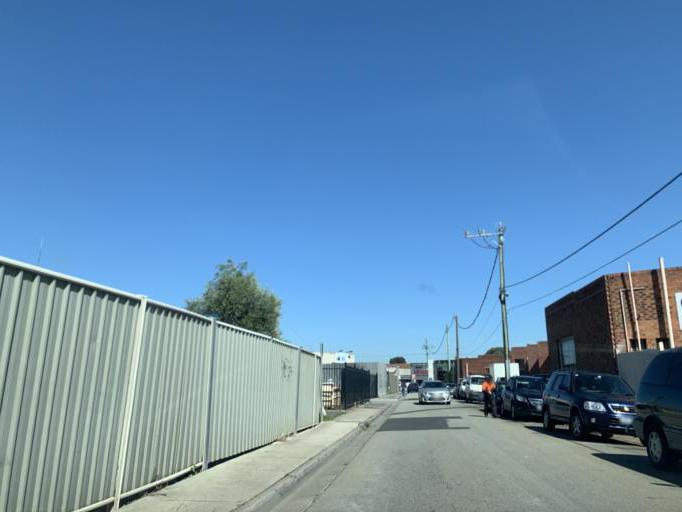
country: AU
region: Victoria
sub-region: Greater Dandenong
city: Dandenong
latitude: -37.9888
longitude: 145.2004
